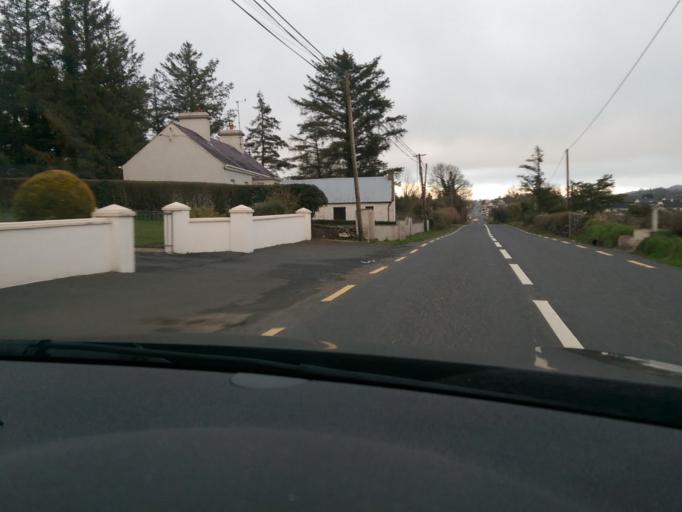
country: IE
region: Connaught
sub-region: Sligo
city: Ballymote
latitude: 53.9997
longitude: -8.5324
